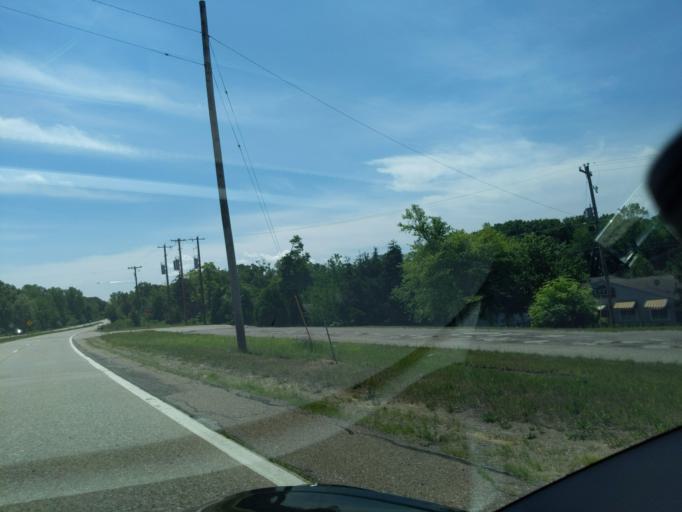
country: US
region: Michigan
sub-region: Kent County
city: Forest Hills
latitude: 42.9530
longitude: -85.4666
